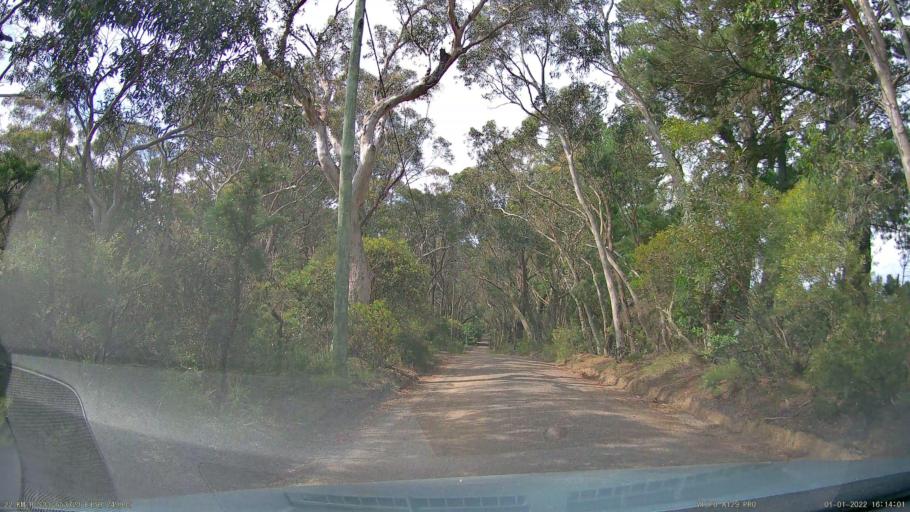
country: AU
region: New South Wales
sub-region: Blue Mountains Municipality
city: Blackheath
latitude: -33.6536
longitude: 150.2499
